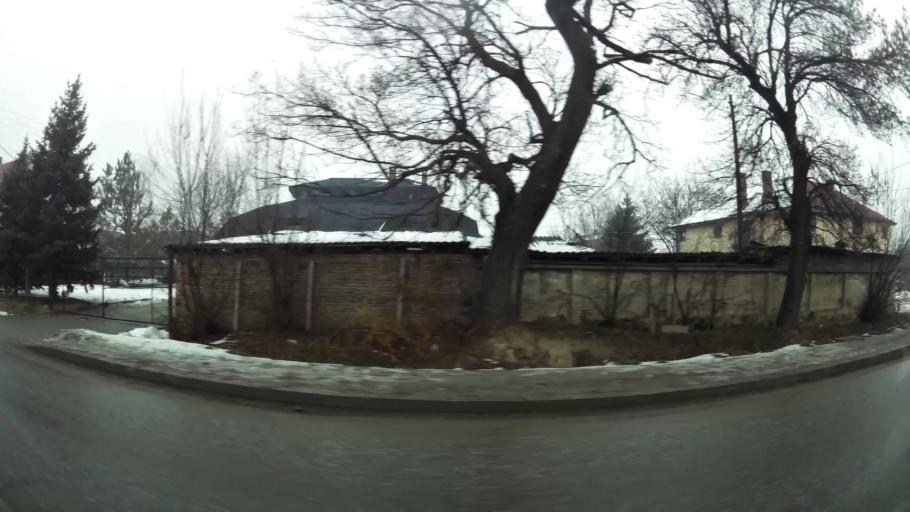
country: MK
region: Petrovec
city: Petrovec
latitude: 41.9367
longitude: 21.6188
